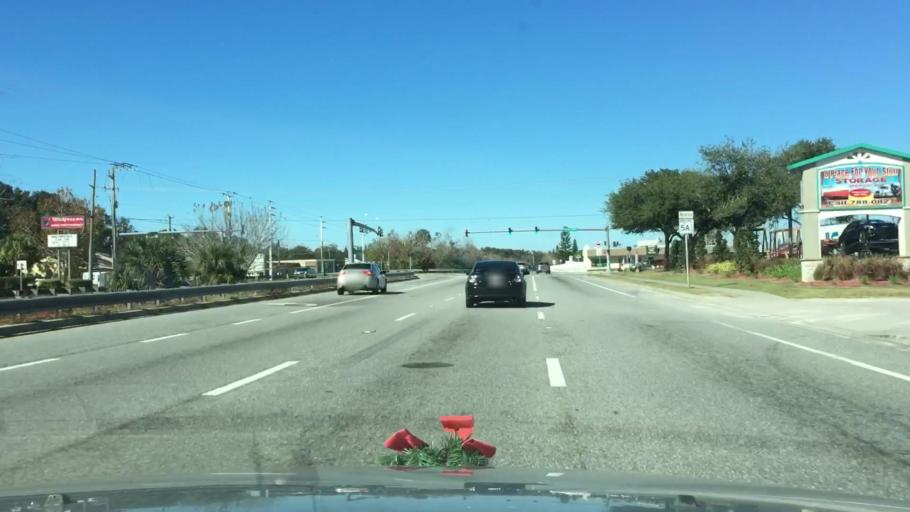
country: US
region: Florida
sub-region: Volusia County
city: South Daytona
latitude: 29.1538
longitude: -81.0191
